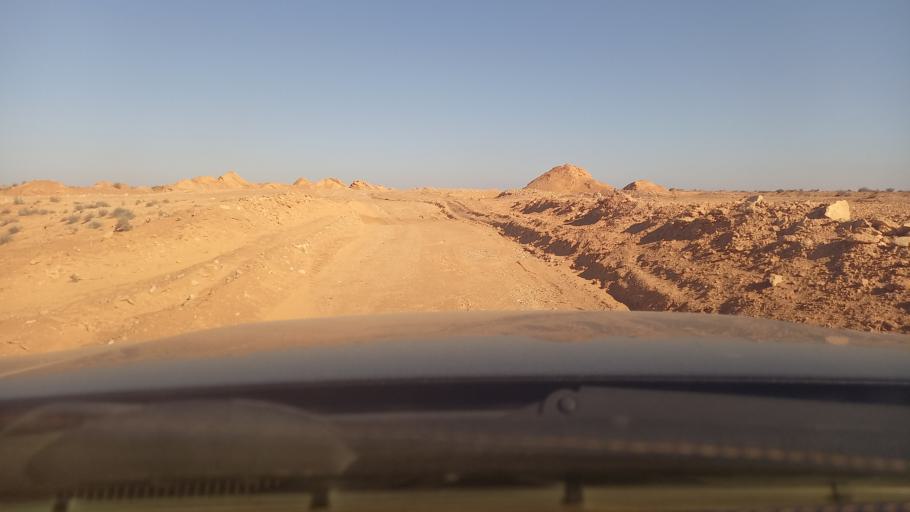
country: TN
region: Madanin
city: Medenine
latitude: 33.1491
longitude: 10.5080
